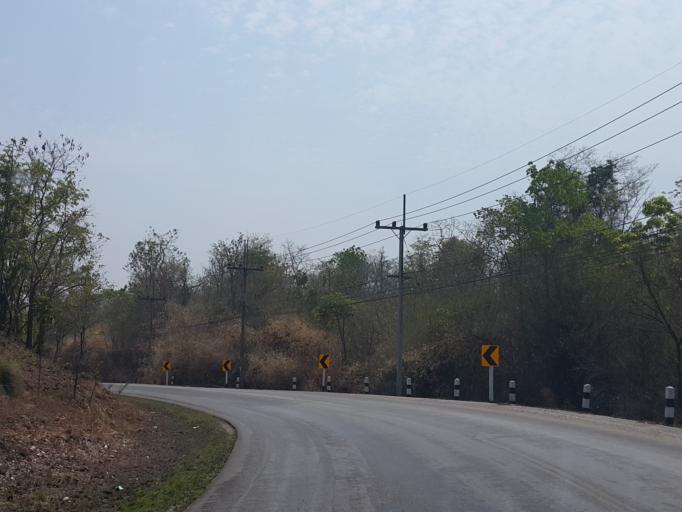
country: TH
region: Lampang
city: Mueang Pan
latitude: 18.7706
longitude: 99.5529
